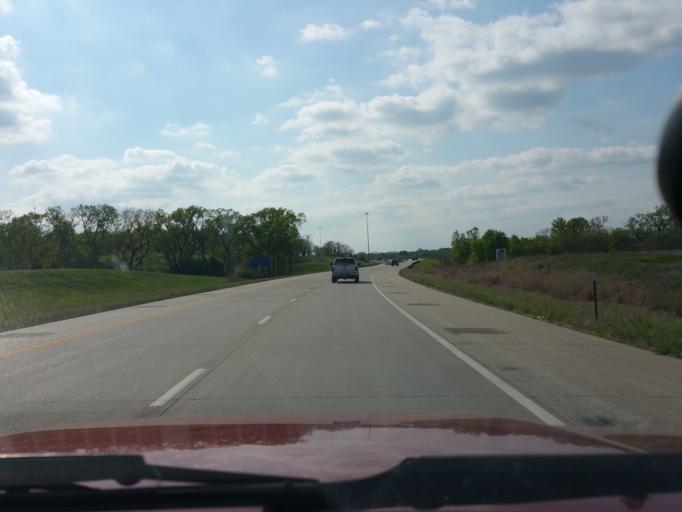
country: US
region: Kansas
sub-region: Pottawatomie County
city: Saint Marys
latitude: 39.0591
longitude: -96.1140
